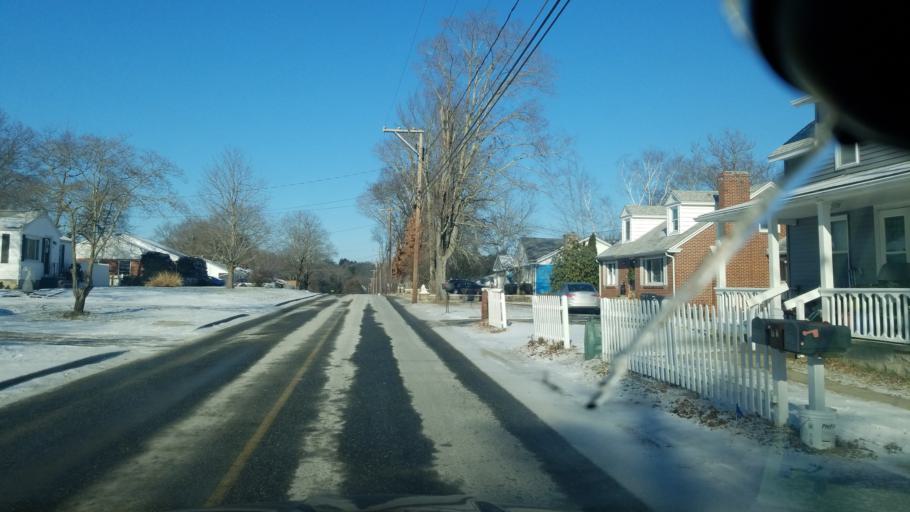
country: US
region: Connecticut
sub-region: Windham County
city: East Brooklyn
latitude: 41.8011
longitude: -71.8996
